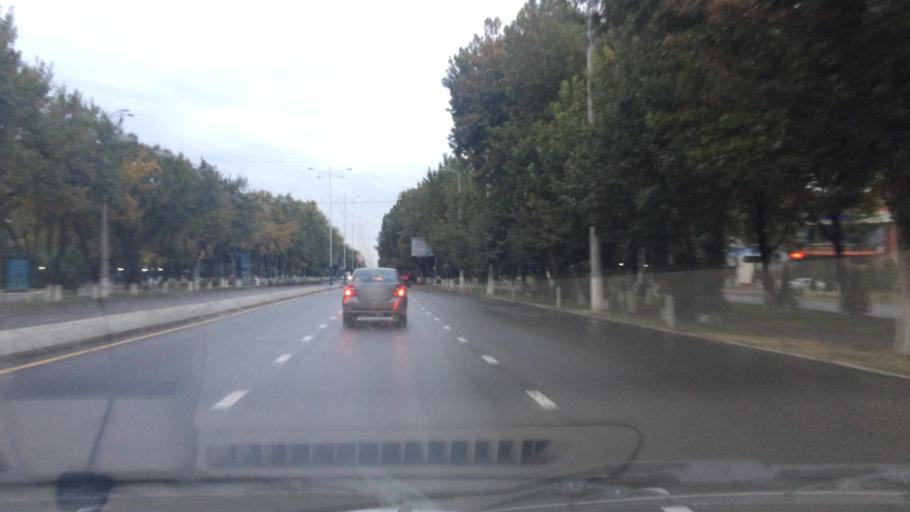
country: UZ
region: Toshkent Shahri
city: Tashkent
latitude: 41.2720
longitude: 69.2029
